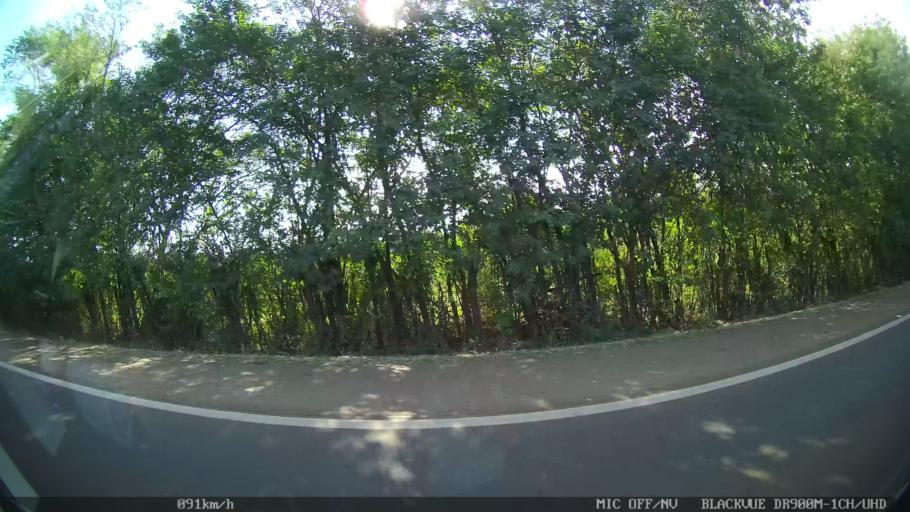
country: BR
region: Sao Paulo
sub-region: Iracemapolis
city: Iracemapolis
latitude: -22.6624
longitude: -47.5306
